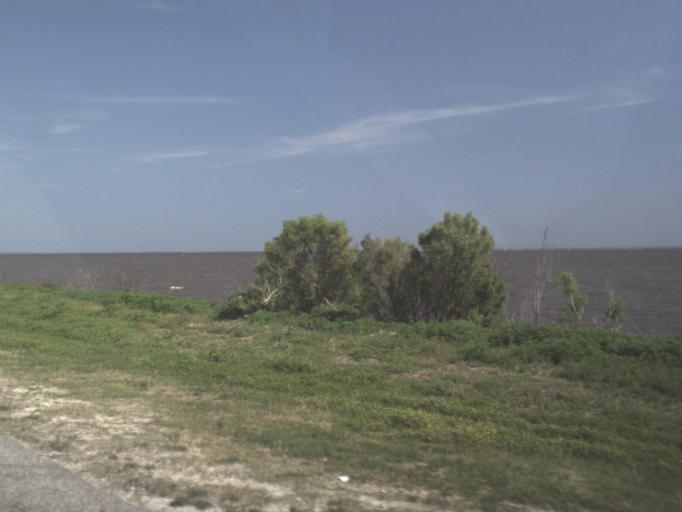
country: US
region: Florida
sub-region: Franklin County
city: Apalachicola
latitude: 29.7270
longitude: -84.9638
